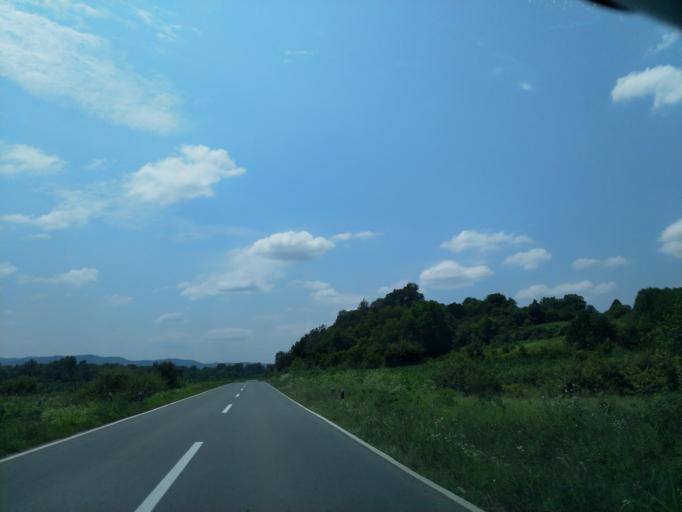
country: RS
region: Central Serbia
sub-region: Rasinski Okrug
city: Krusevac
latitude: 43.4839
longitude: 21.2752
